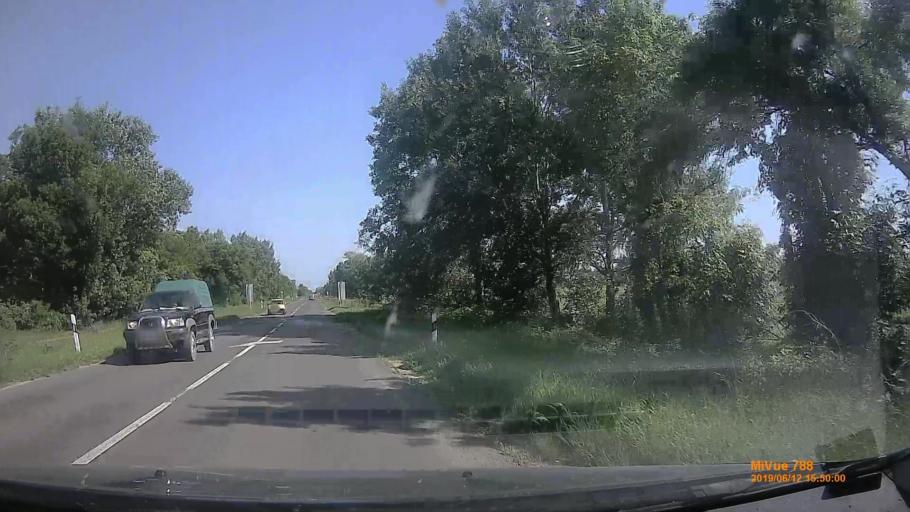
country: HU
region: Csongrad
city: Apatfalva
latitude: 46.1905
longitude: 20.5622
